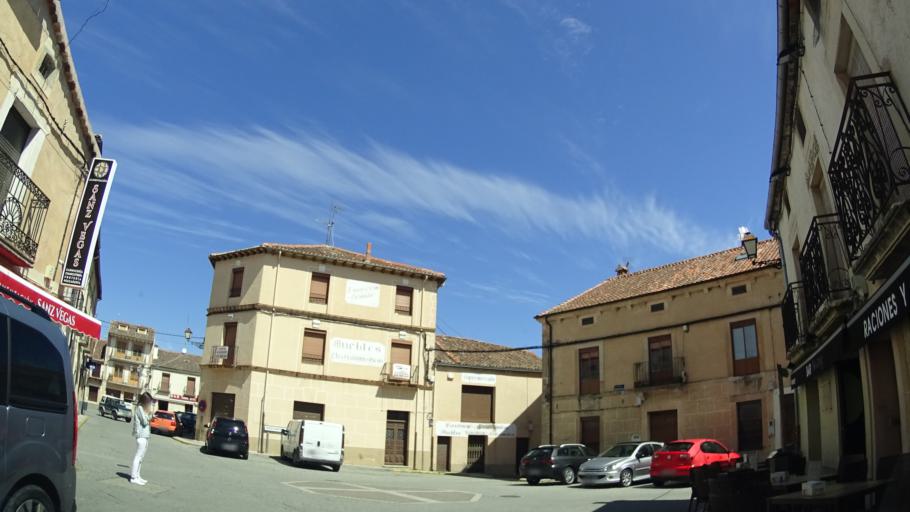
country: ES
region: Castille and Leon
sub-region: Provincia de Segovia
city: Pradena
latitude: 41.1387
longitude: -3.6881
